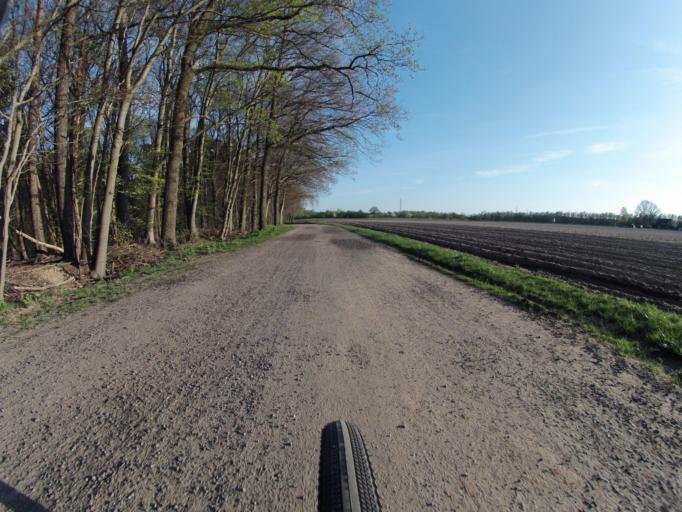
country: DE
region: Lower Saxony
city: Salzbergen
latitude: 52.3472
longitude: 7.3417
